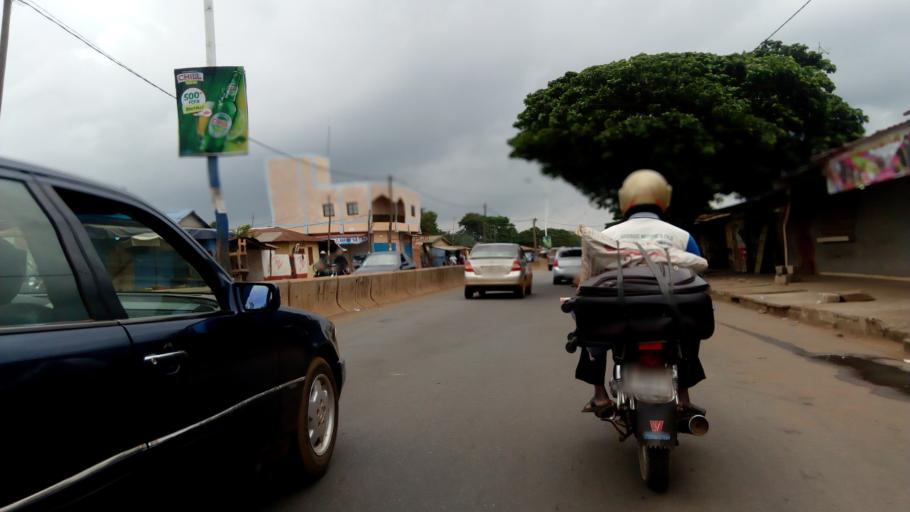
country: TG
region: Maritime
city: Lome
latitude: 6.2227
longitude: 1.2094
